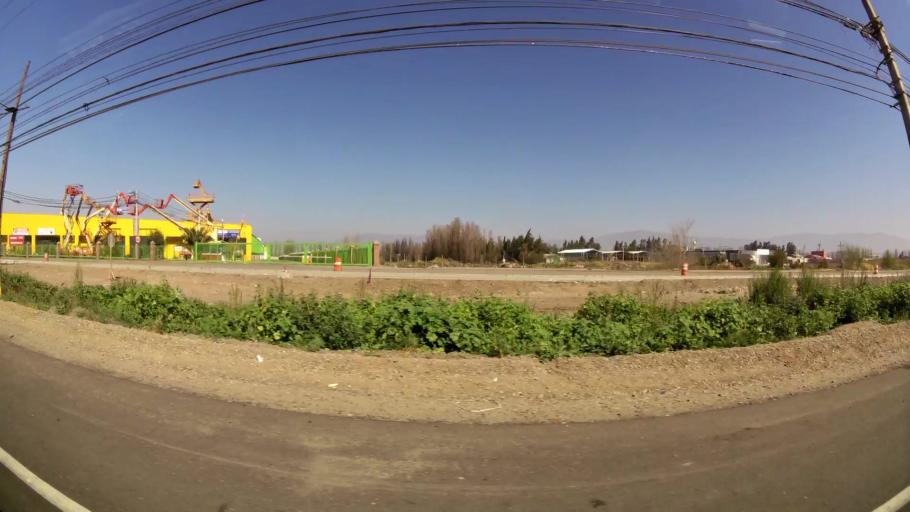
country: CL
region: Santiago Metropolitan
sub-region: Provincia de Chacabuco
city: Chicureo Abajo
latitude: -33.2908
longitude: -70.7343
